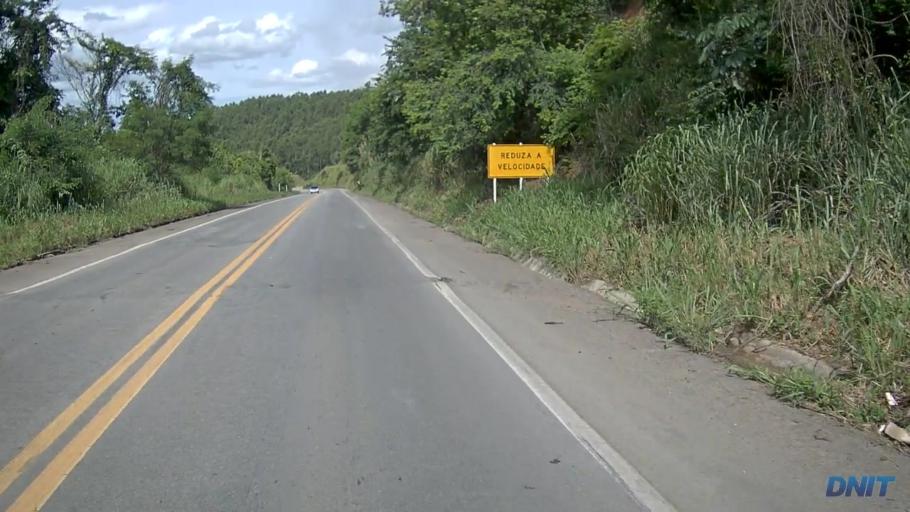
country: BR
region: Minas Gerais
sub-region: Ipaba
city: Ipaba
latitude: -19.3237
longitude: -42.4115
